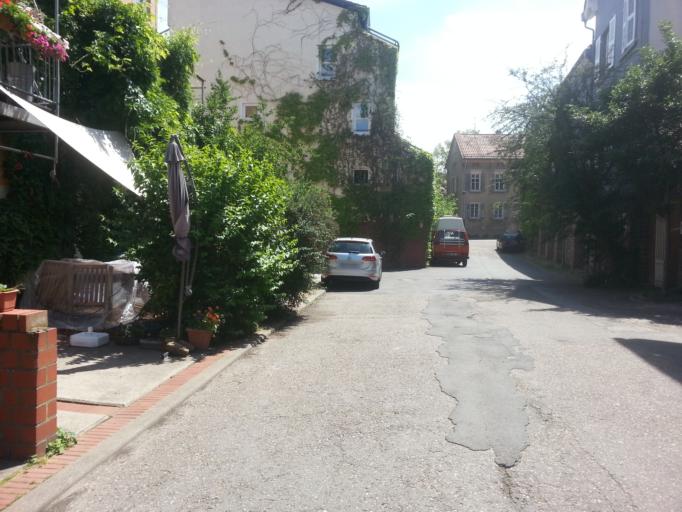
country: DE
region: Baden-Wuerttemberg
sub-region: Karlsruhe Region
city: Eppelheim
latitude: 49.4244
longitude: 8.6514
